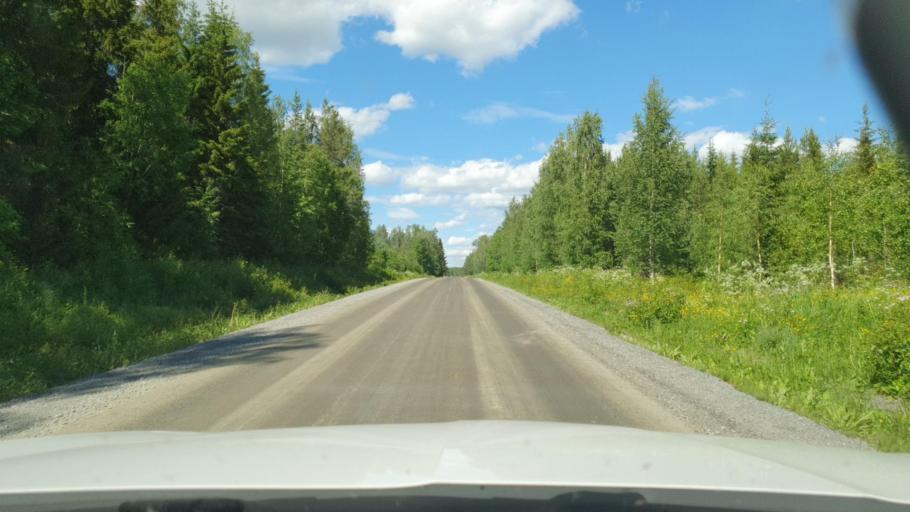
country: SE
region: Vaesterbotten
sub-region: Skelleftea Kommun
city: Forsbacka
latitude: 64.7809
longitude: 20.5144
